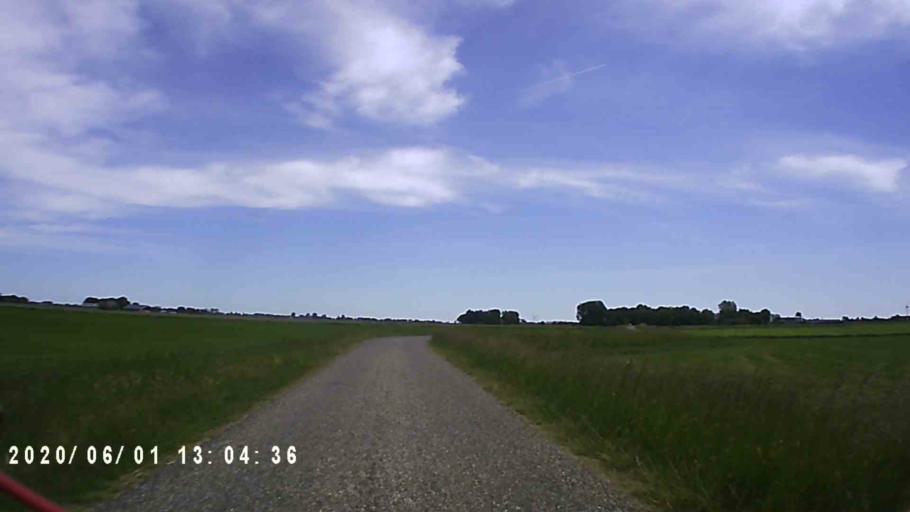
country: NL
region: Friesland
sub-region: Gemeente Franekeradeel
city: Tzum
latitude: 53.1423
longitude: 5.5383
